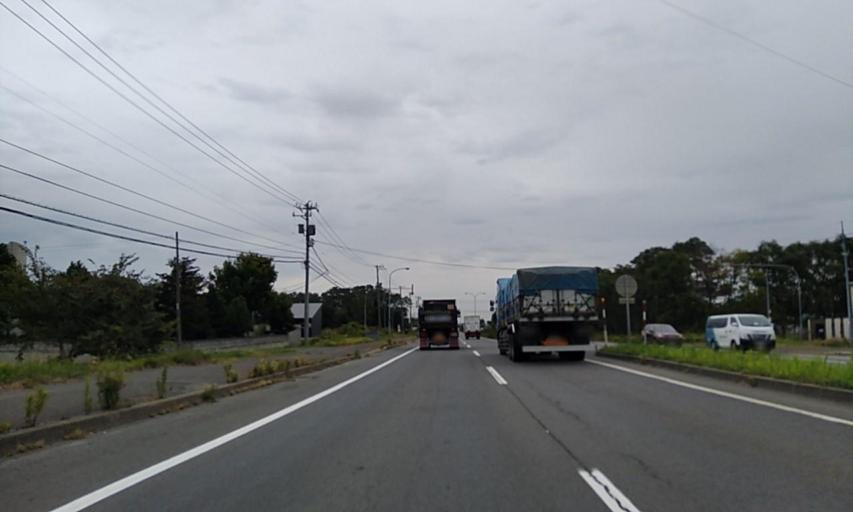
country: JP
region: Hokkaido
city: Sapporo
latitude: 43.1451
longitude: 141.2097
